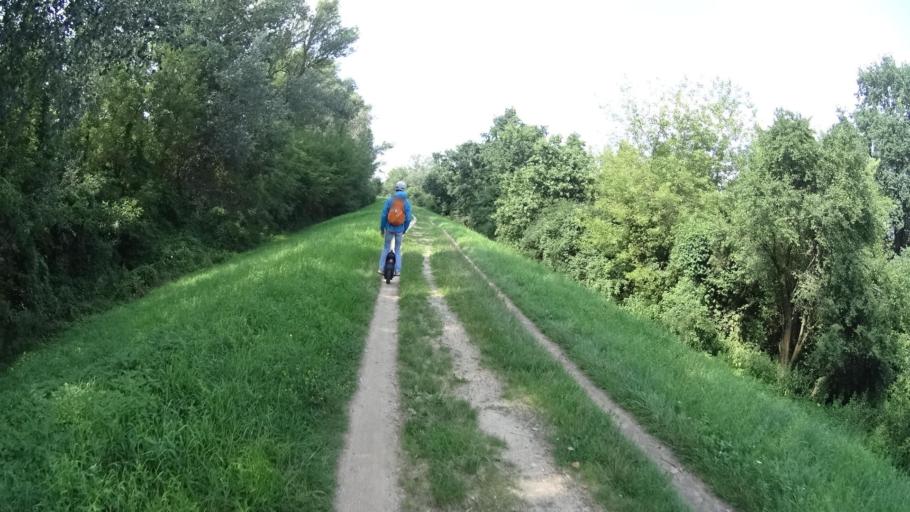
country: PL
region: Masovian Voivodeship
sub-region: Powiat legionowski
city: Jablonna
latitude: 52.3615
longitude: 20.9192
